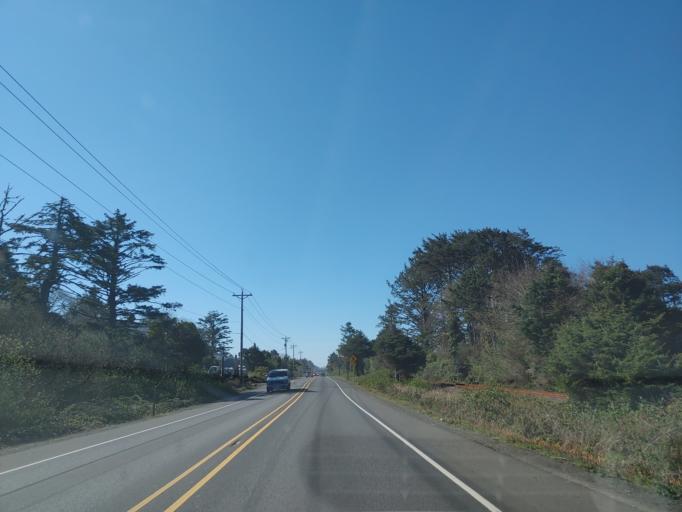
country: US
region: Oregon
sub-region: Tillamook County
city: Rockaway Beach
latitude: 45.6019
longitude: -123.9458
